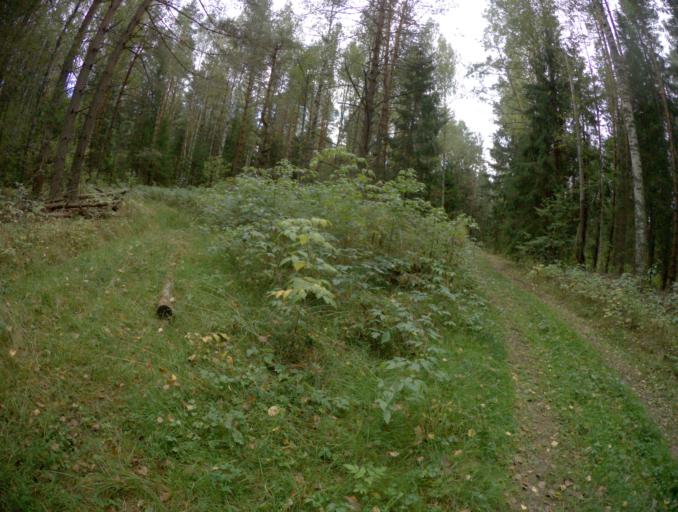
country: RU
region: Vladimir
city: Golovino
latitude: 55.8908
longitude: 40.4372
